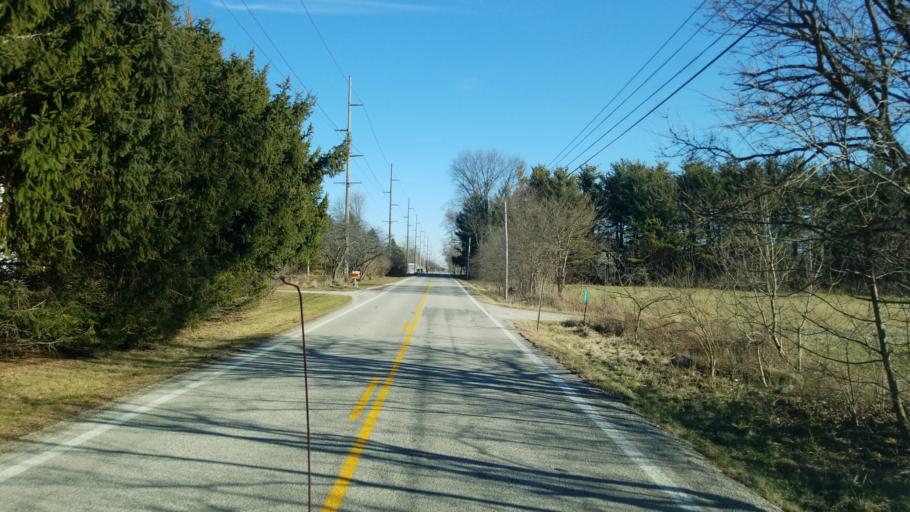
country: US
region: Ohio
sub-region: Wood County
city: Pemberville
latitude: 41.4500
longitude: -83.4417
